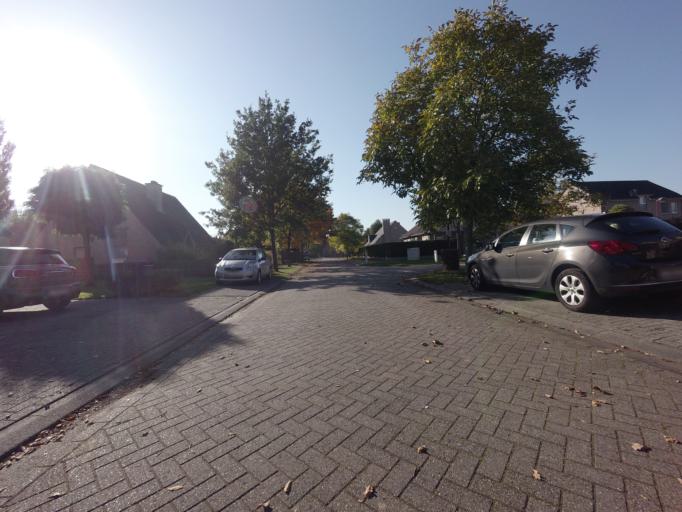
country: BE
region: Flanders
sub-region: Provincie Antwerpen
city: Lint
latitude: 51.1214
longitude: 4.4884
